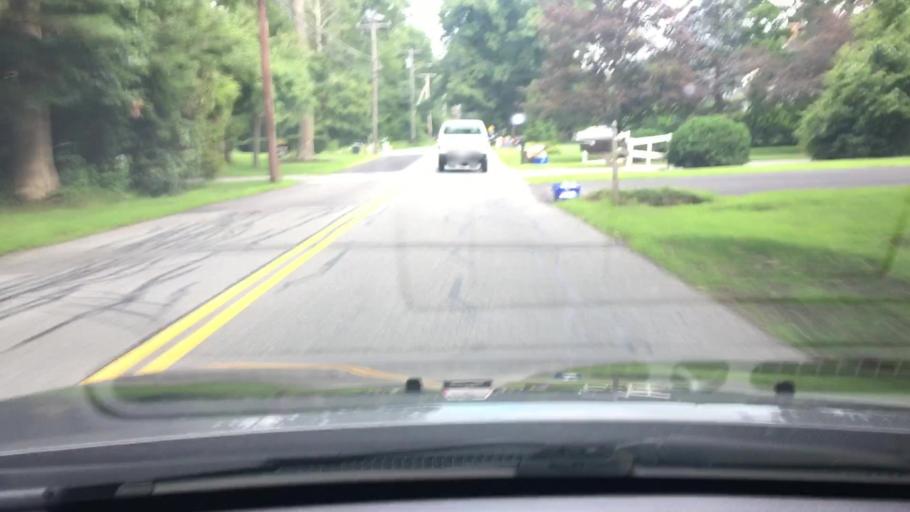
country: US
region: Massachusetts
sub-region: Worcester County
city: Hopedale
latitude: 42.1636
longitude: -71.5408
